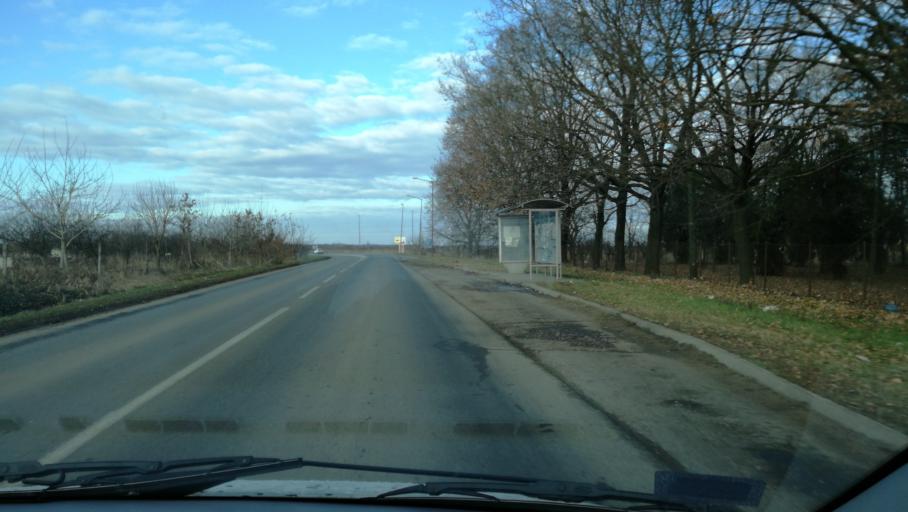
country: RS
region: Autonomna Pokrajina Vojvodina
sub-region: Severnobanatski Okrug
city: Kikinda
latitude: 45.8228
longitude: 20.4305
